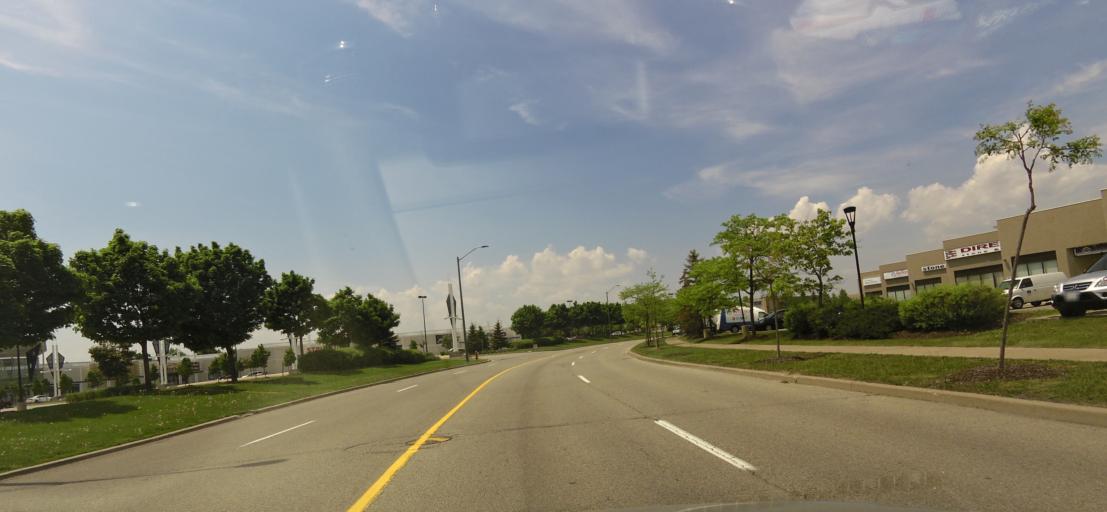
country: CA
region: Ontario
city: Oakville
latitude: 43.5155
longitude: -79.6930
